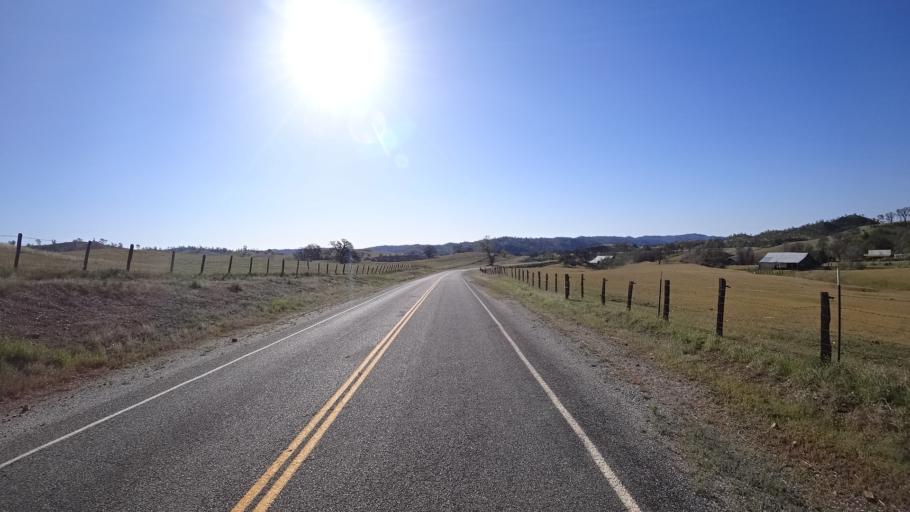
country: US
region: California
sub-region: Glenn County
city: Orland
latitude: 39.6860
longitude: -122.5404
